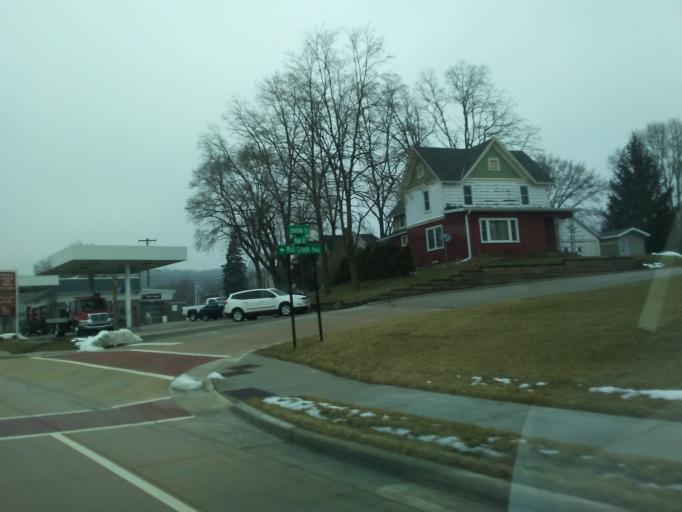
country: US
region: Wisconsin
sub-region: Dane County
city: Cross Plains
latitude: 43.1125
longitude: -89.6472
